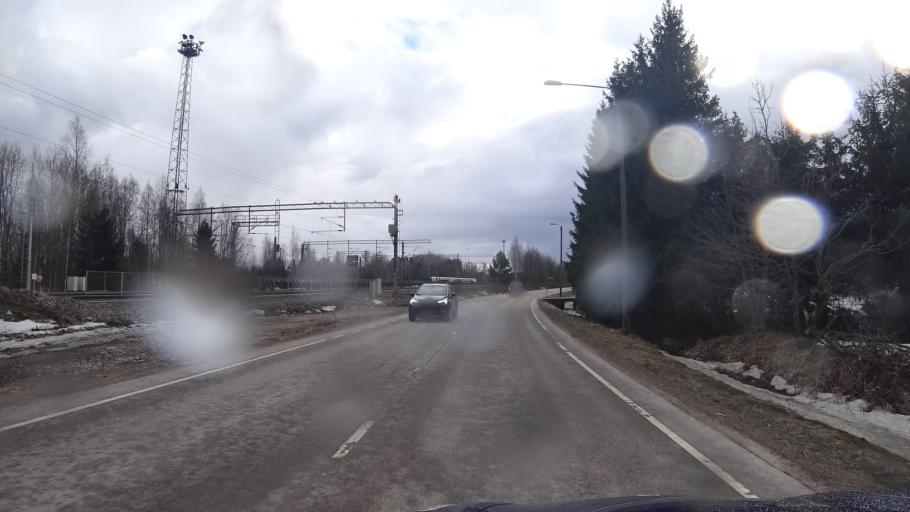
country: FI
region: Kymenlaakso
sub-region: Kotka-Hamina
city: Karhula
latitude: 60.5436
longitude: 26.9123
